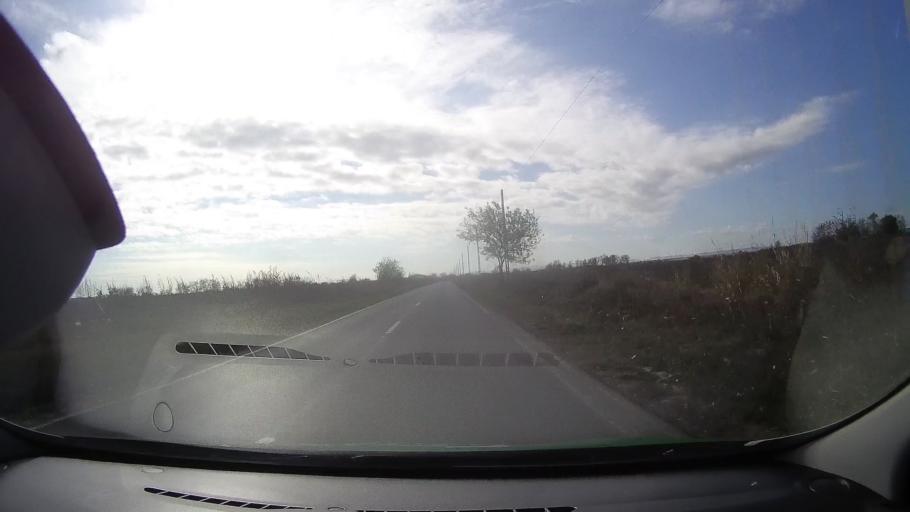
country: RO
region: Tulcea
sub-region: Comuna Sarichioi
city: Sarichioi
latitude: 44.9842
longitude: 28.8839
